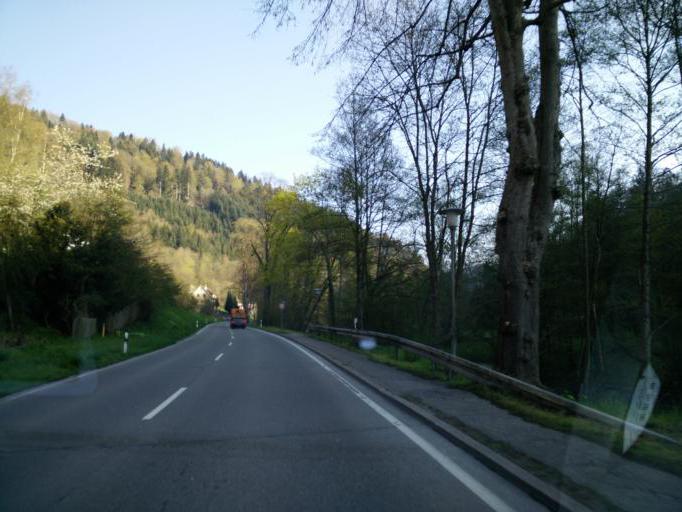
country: DE
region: Baden-Wuerttemberg
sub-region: Karlsruhe Region
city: Bad Liebenzell
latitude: 48.7627
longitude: 8.7294
